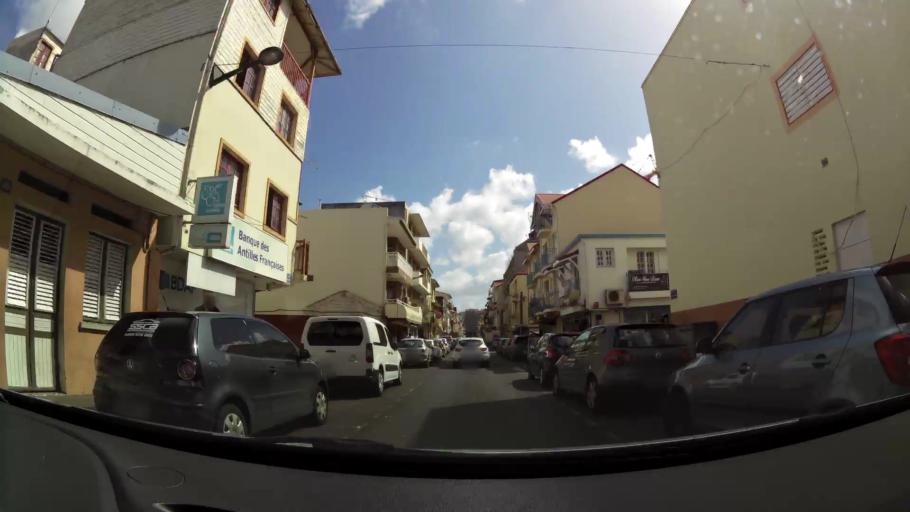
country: MQ
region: Martinique
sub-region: Martinique
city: Fort-de-France
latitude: 14.6112
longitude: -61.0712
